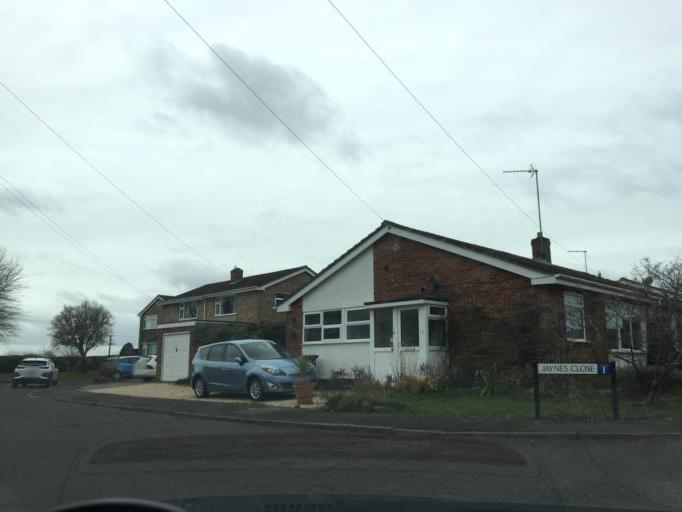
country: GB
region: England
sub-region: Oxfordshire
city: Banbury
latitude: 52.0444
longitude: -1.3368
